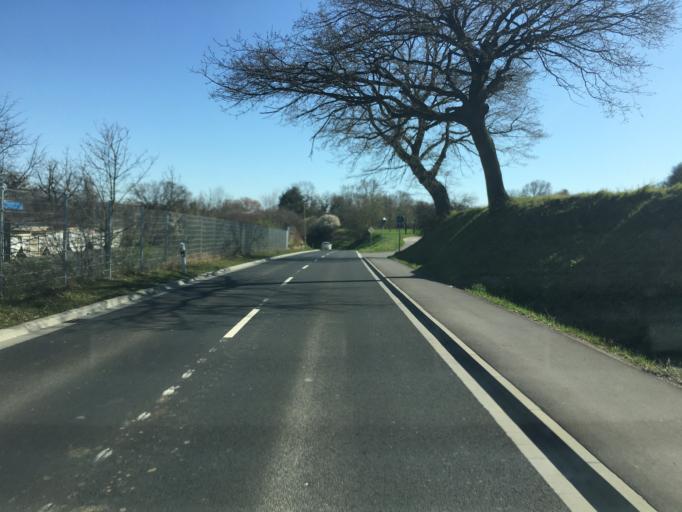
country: DE
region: North Rhine-Westphalia
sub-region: Regierungsbezirk Koln
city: Kreuzau
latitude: 50.7527
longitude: 6.4783
